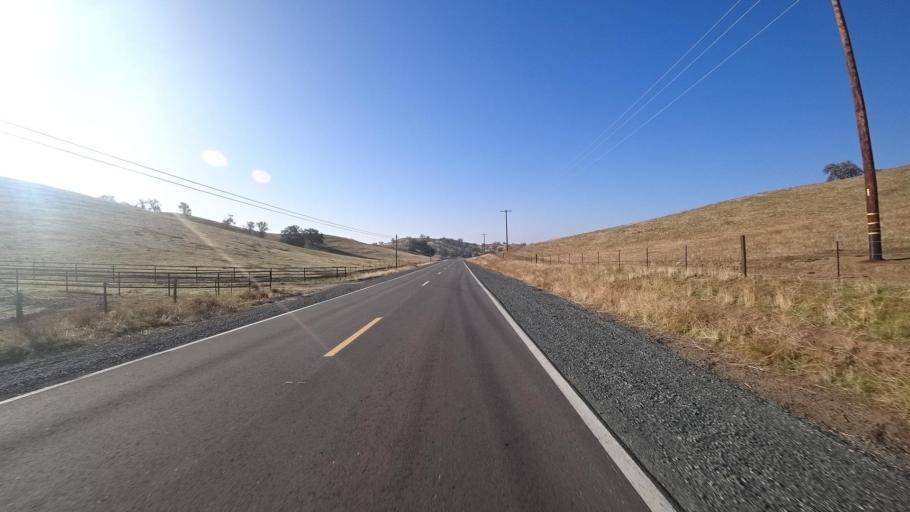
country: US
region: California
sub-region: Tulare County
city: Richgrove
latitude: 35.7207
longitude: -118.8591
